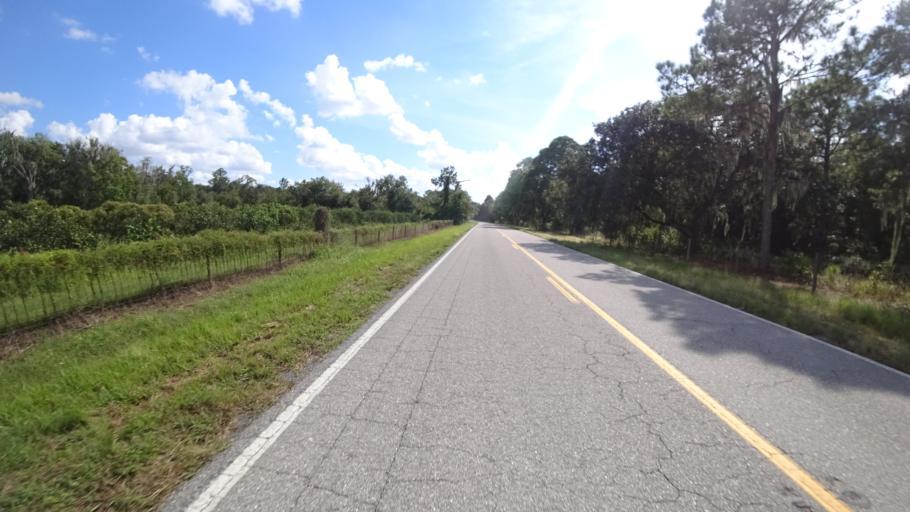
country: US
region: Florida
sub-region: Hillsborough County
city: Wimauma
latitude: 27.5419
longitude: -82.1039
